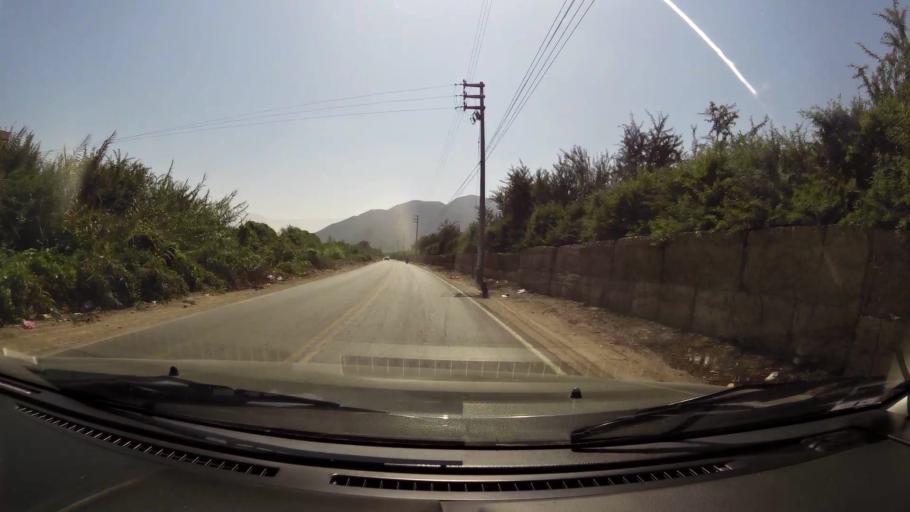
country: PE
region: Ica
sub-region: Provincia de Ica
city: San Juan Bautista
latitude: -13.9894
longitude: -75.6952
